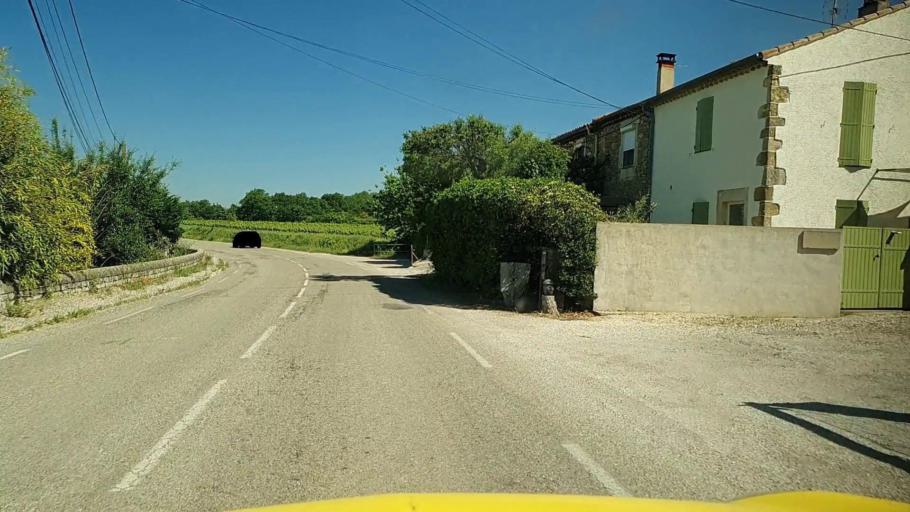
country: FR
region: Languedoc-Roussillon
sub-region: Departement du Gard
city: Moussac
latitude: 43.9837
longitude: 4.2306
